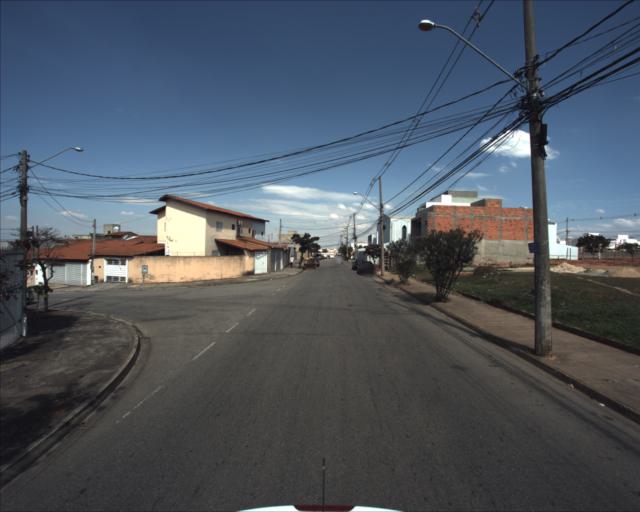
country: BR
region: Sao Paulo
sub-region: Sorocaba
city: Sorocaba
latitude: -23.4821
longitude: -47.5106
